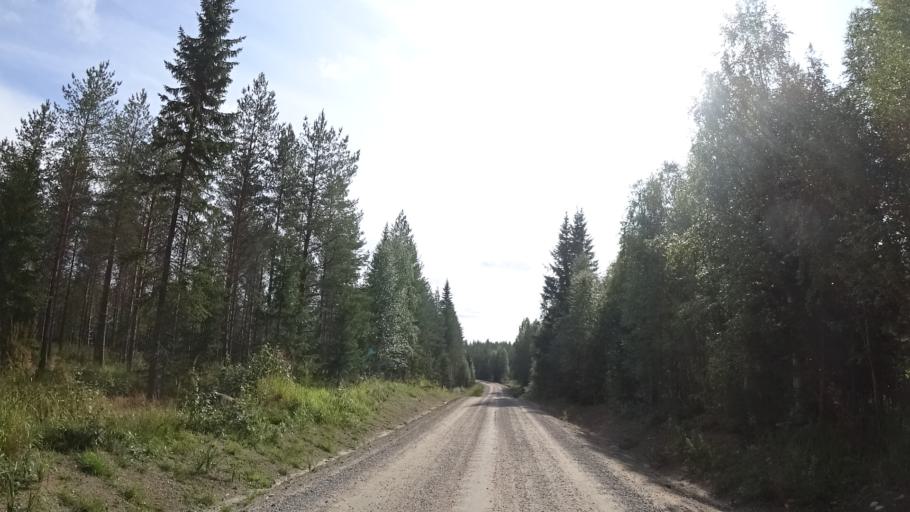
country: FI
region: North Karelia
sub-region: Pielisen Karjala
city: Lieksa
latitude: 63.5932
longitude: 30.1376
